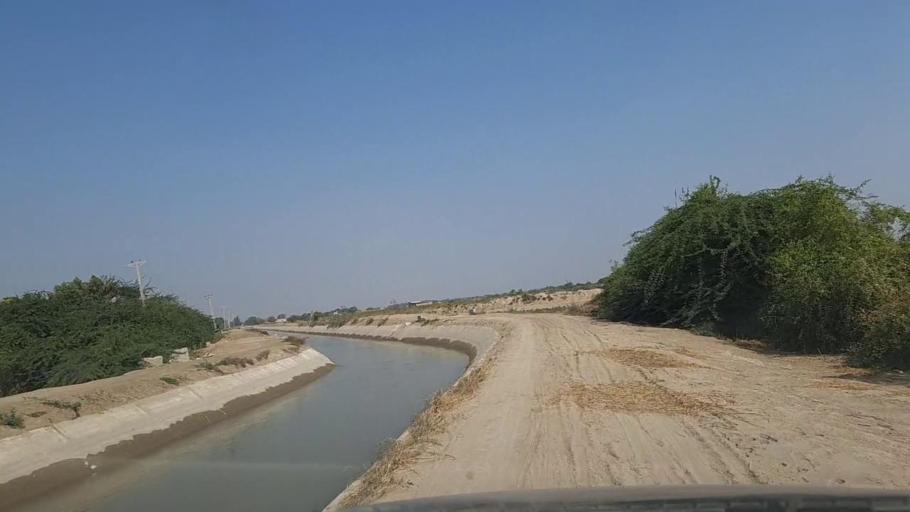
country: PK
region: Sindh
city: Mirpur Sakro
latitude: 24.5245
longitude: 67.8106
